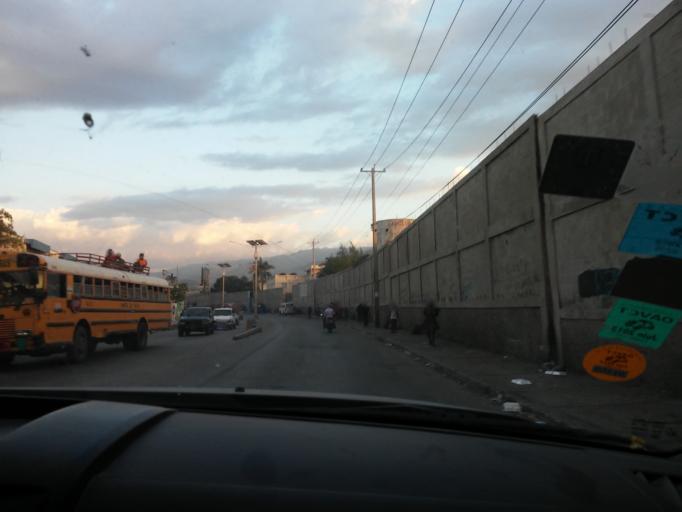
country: HT
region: Ouest
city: Port-au-Prince
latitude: 18.5619
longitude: -72.3405
